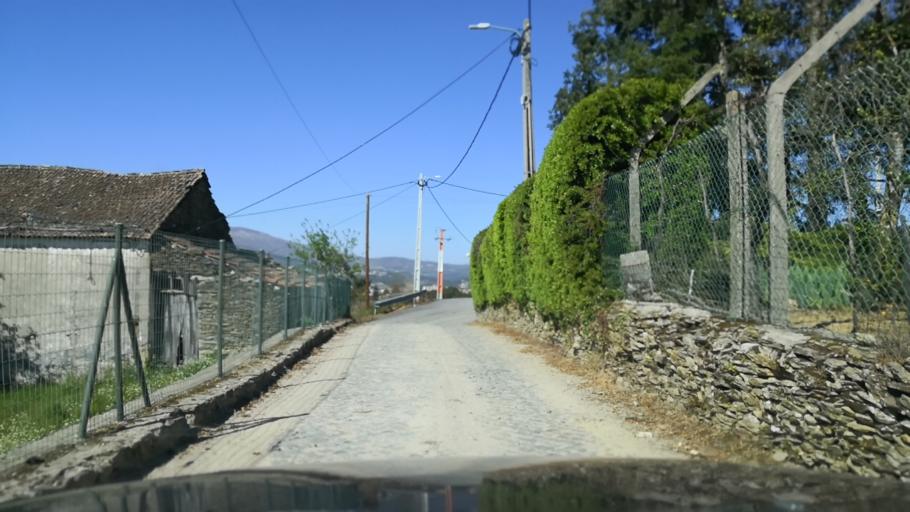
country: PT
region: Vila Real
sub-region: Vila Real
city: Vila Real
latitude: 41.2756
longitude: -7.7292
